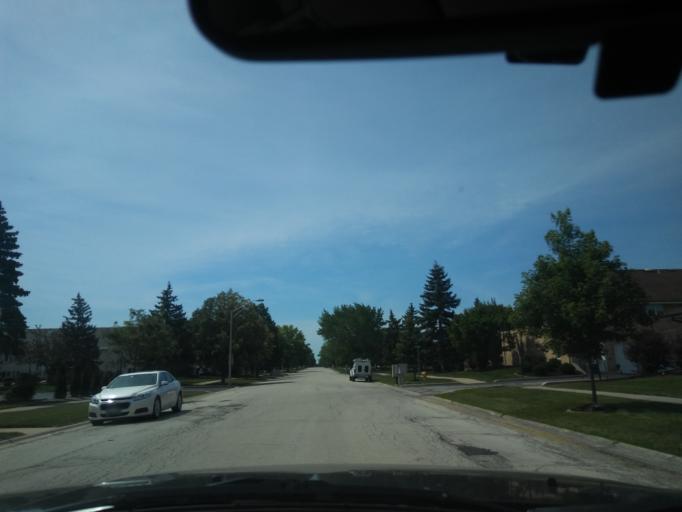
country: US
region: Illinois
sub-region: Cook County
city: Tinley Park
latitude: 41.6146
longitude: -87.7968
